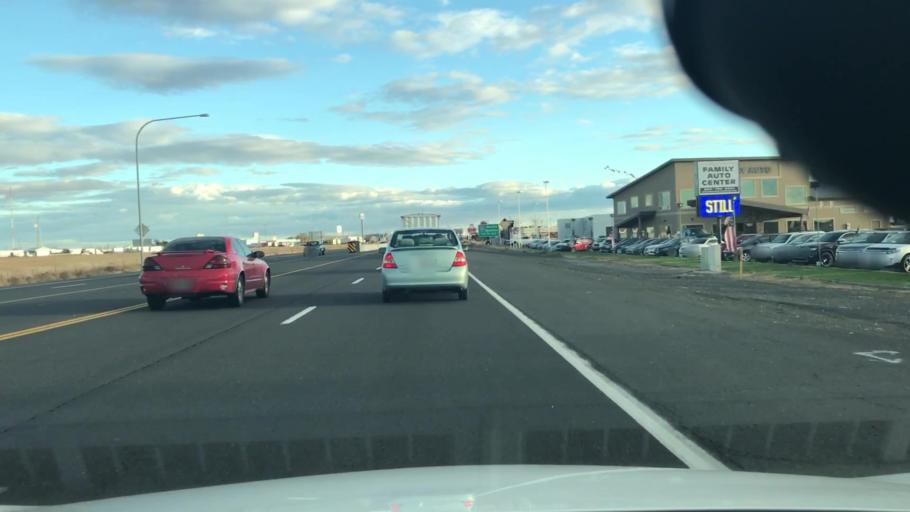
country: US
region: Washington
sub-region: Grant County
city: Moses Lake
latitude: 47.1057
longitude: -119.2516
